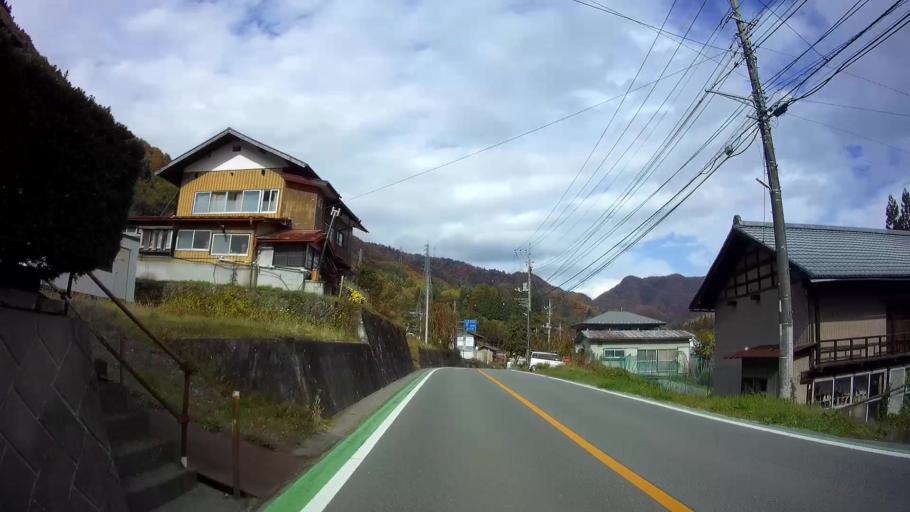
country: JP
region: Gunma
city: Nakanojomachi
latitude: 36.5986
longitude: 138.6283
